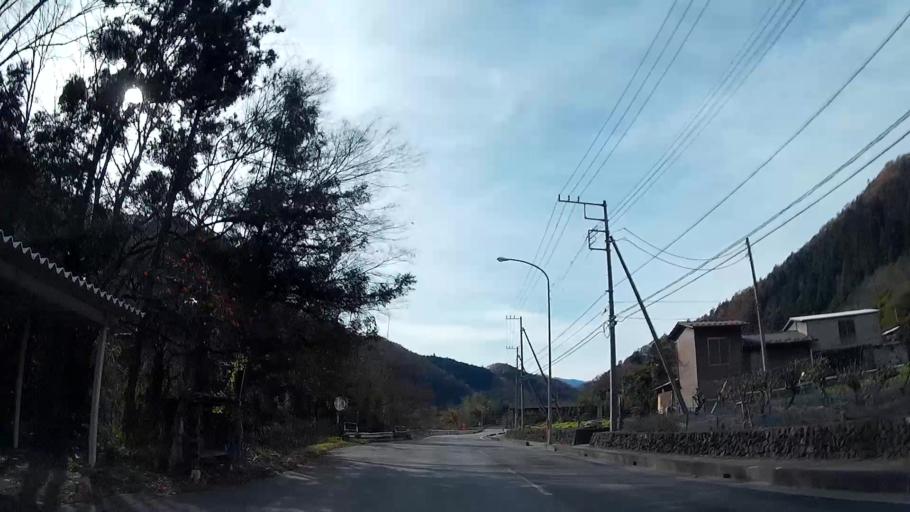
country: JP
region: Saitama
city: Chichibu
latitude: 36.0492
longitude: 139.0049
